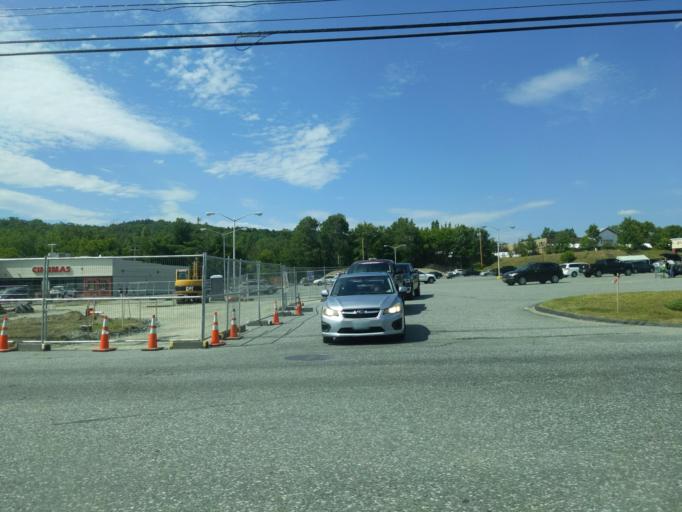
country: US
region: Vermont
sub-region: Windsor County
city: White River Junction
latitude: 43.6362
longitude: -72.2890
